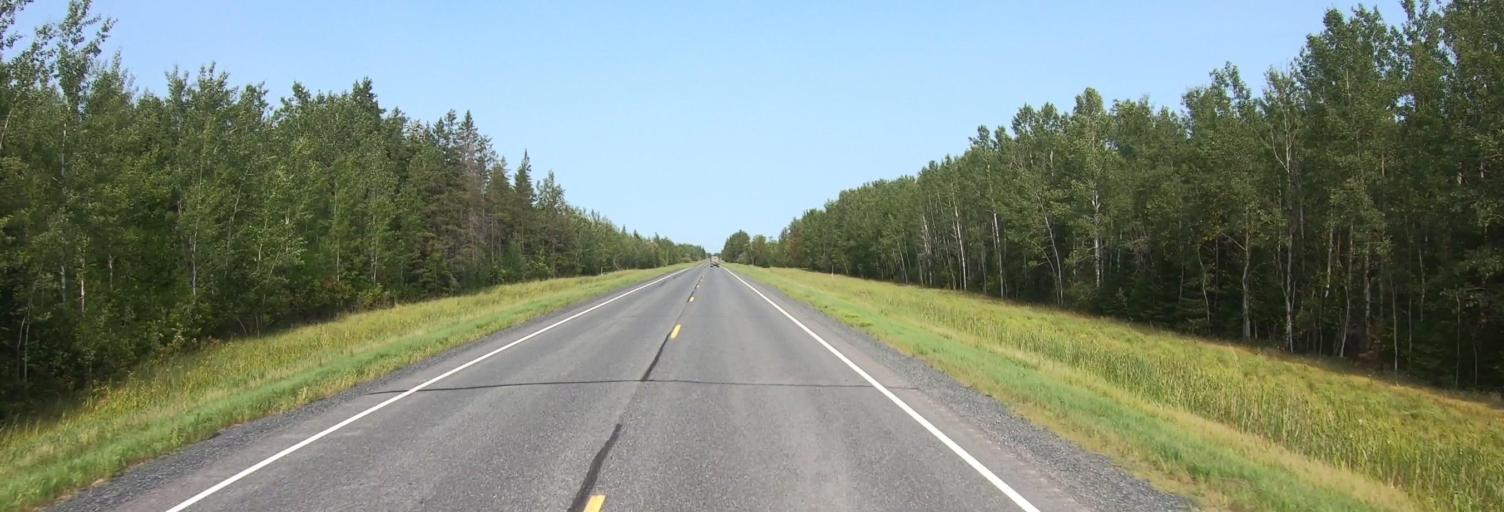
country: US
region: Minnesota
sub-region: Koochiching County
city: International Falls
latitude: 48.5634
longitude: -93.8181
